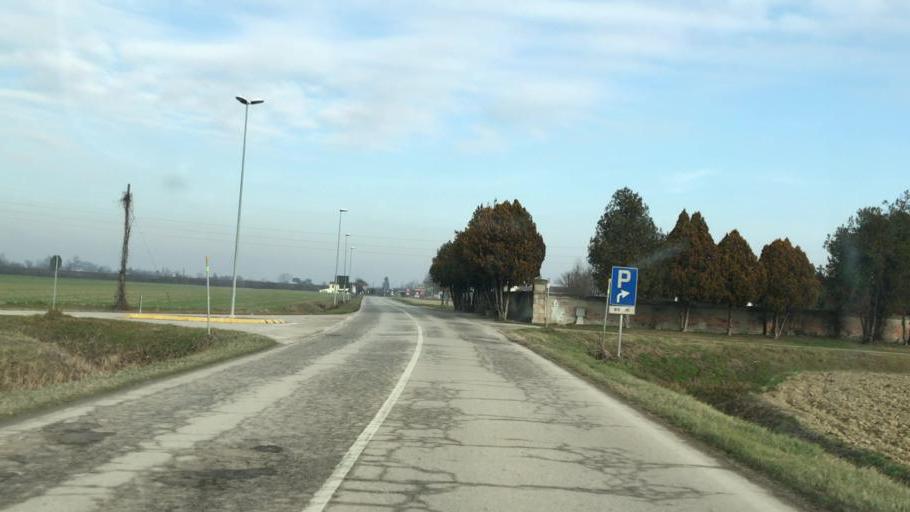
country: IT
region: Veneto
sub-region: Provincia di Rovigo
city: Fratta Polesine
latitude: 45.0332
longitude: 11.6507
